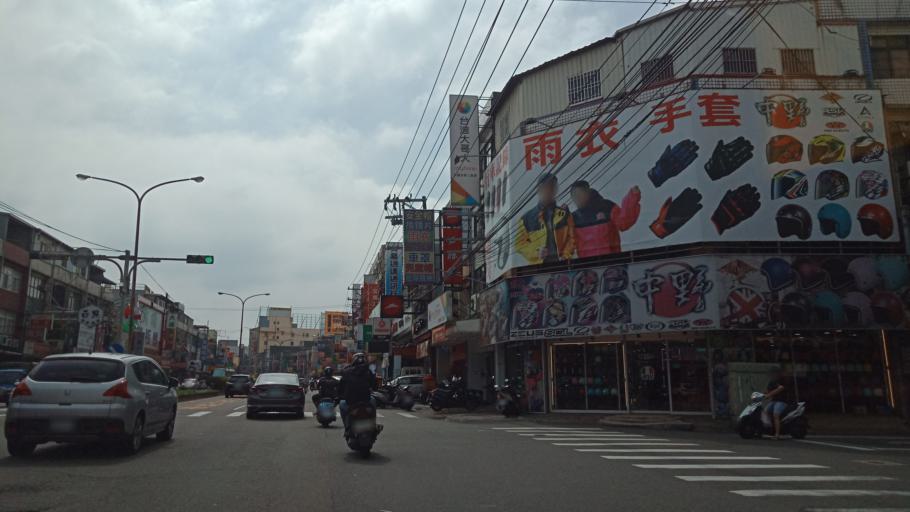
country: TW
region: Taiwan
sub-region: Hsinchu
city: Zhubei
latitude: 24.8688
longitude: 120.9950
